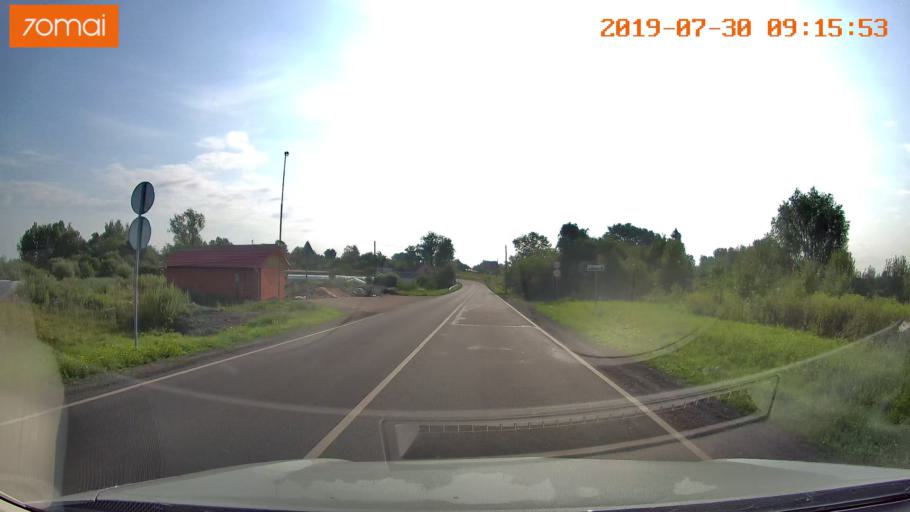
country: RU
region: Kaliningrad
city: Nesterov
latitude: 54.6338
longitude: 22.5491
